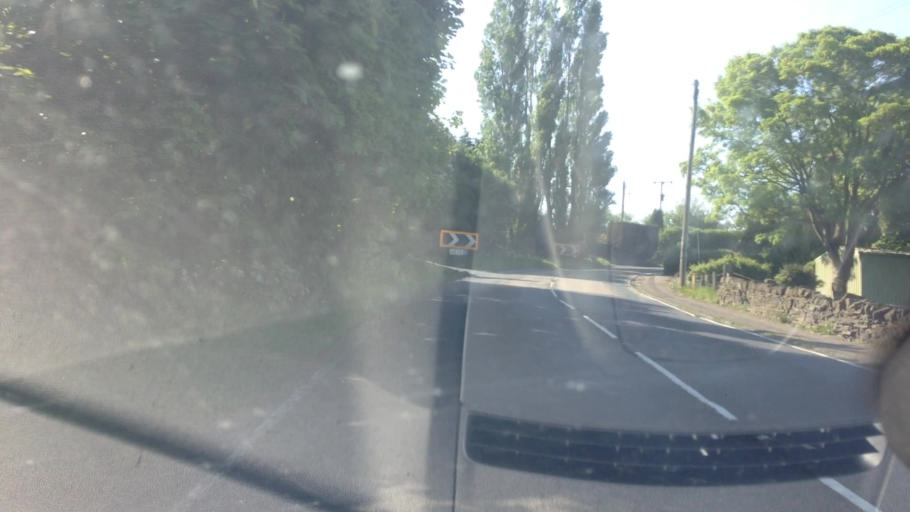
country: GB
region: England
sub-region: Kirklees
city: Mirfield
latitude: 53.6743
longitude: -1.7283
